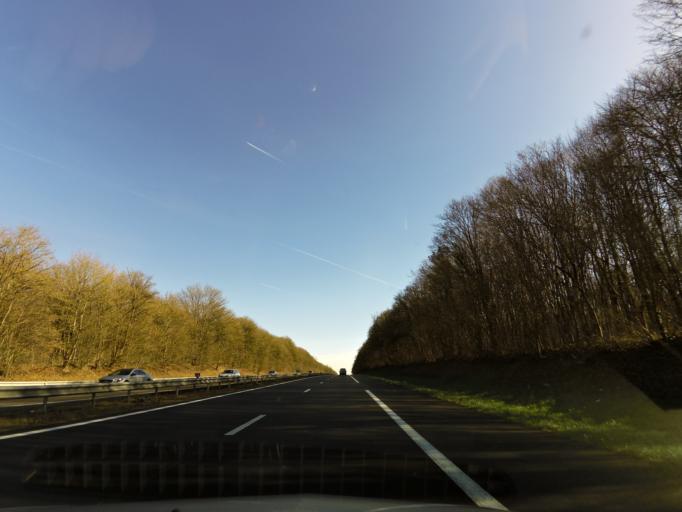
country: FR
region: Bourgogne
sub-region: Departement de l'Yonne
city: Vermenton
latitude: 47.7120
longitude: 3.7803
